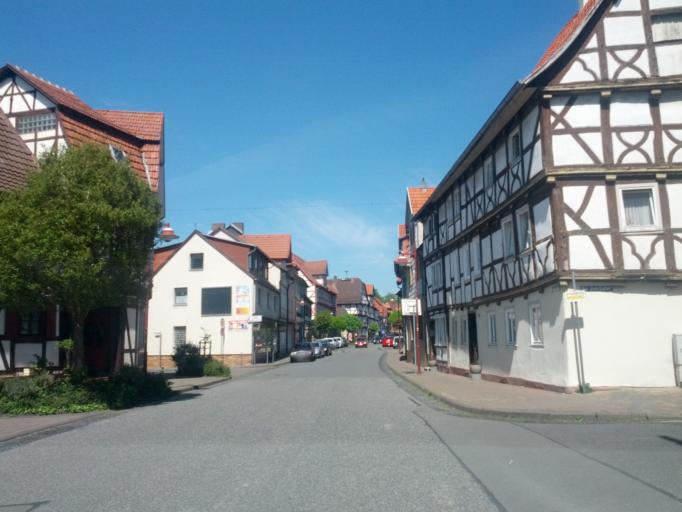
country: DE
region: Hesse
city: Wanfried
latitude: 51.1812
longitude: 10.1713
